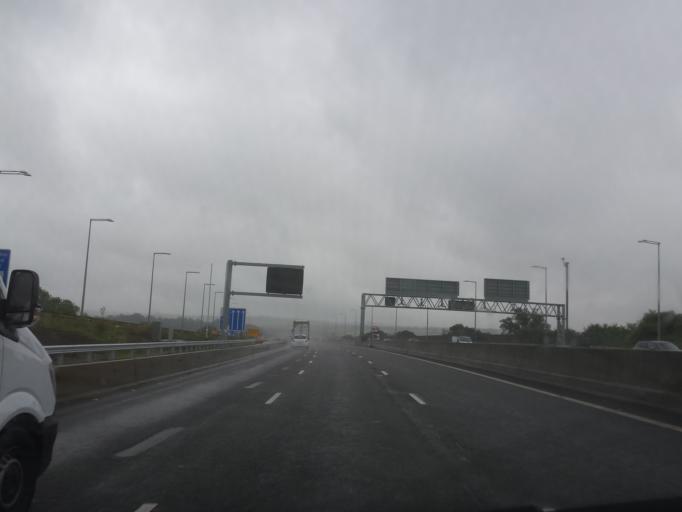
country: GB
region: England
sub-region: Derbyshire
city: Pinxton
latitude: 53.0994
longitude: -1.3206
